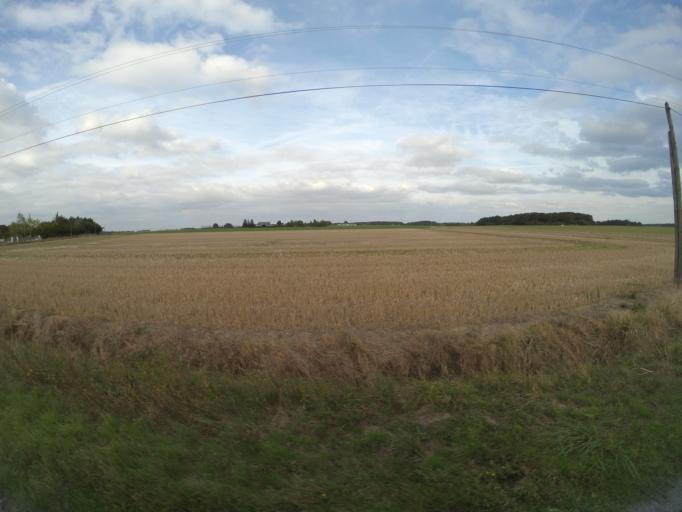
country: FR
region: Centre
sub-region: Departement d'Indre-et-Loire
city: Reugny
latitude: 47.4742
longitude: 0.9032
